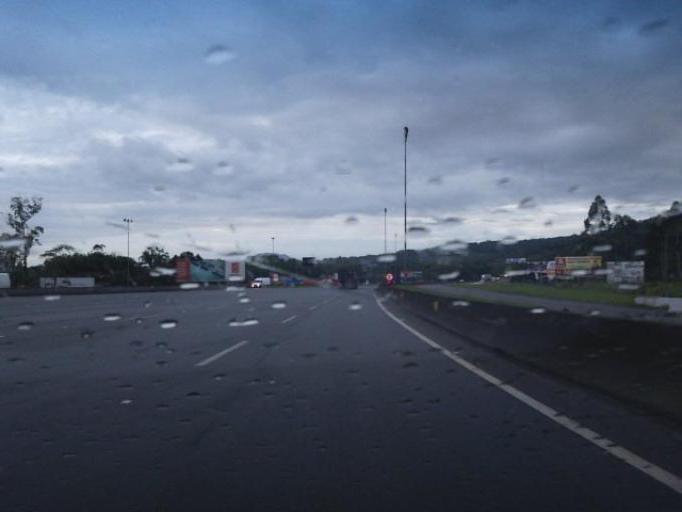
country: BR
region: Santa Catarina
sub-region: Joinville
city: Joinville
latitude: -25.9932
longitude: -48.8810
